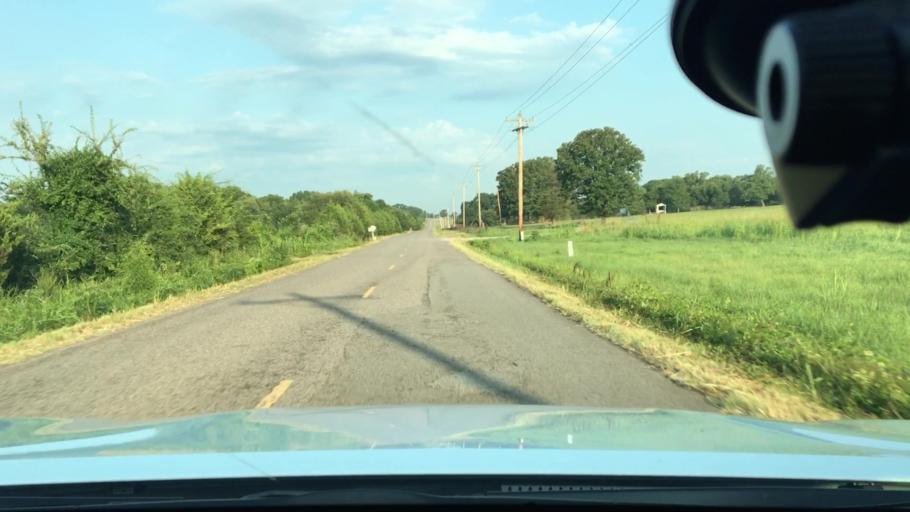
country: US
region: Arkansas
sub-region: Johnson County
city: Coal Hill
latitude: 35.3663
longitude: -93.6058
